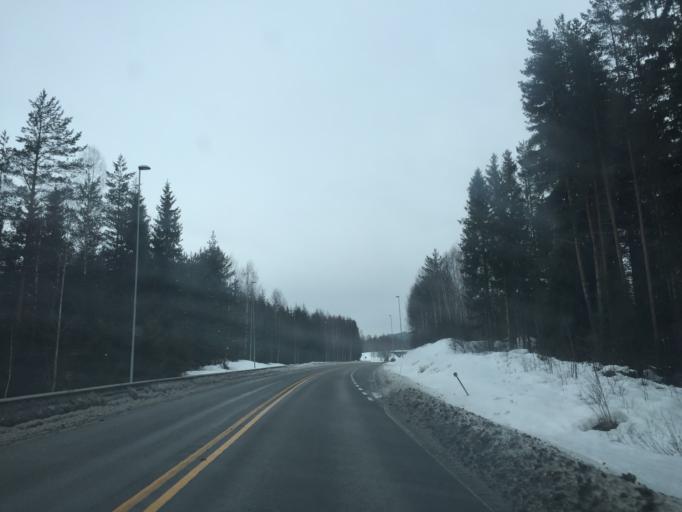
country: NO
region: Hedmark
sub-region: Stange
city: Stange
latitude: 60.7271
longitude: 11.2919
